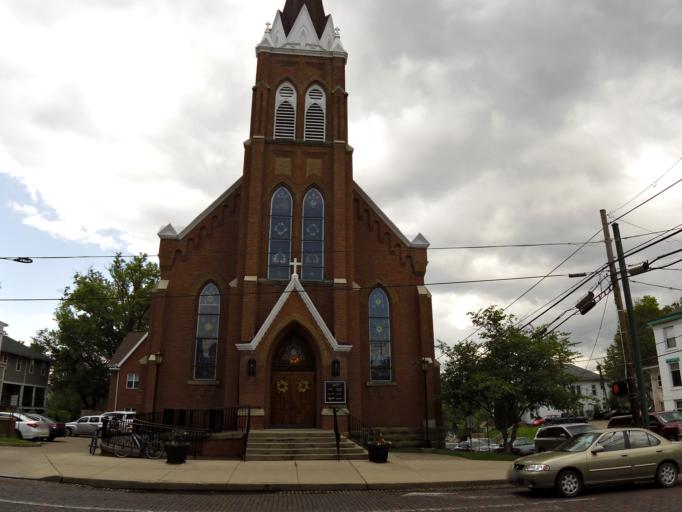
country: US
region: Ohio
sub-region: Athens County
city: Athens
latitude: 39.3305
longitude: -82.0997
